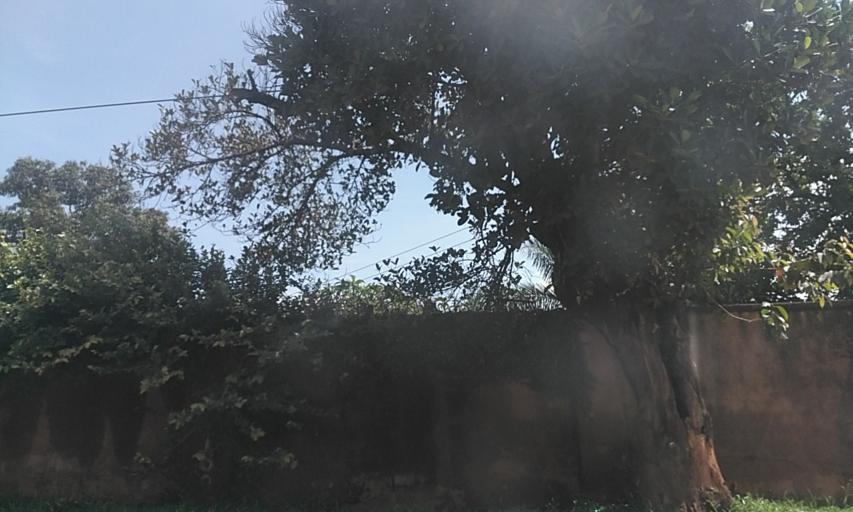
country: UG
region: Central Region
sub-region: Kampala District
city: Kampala
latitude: 0.3241
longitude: 32.6014
